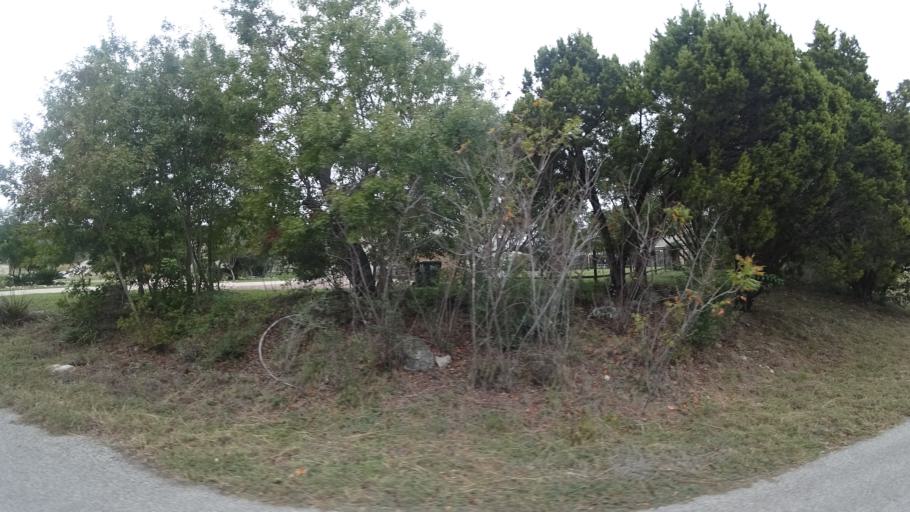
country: US
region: Texas
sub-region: Travis County
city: Hudson Bend
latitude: 30.3717
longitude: -97.9281
